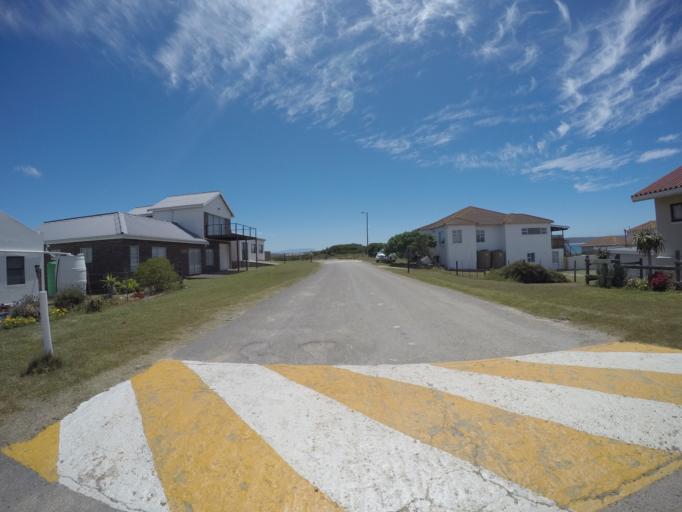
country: ZA
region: Western Cape
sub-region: Eden District Municipality
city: Riversdale
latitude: -34.4203
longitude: 20.8544
